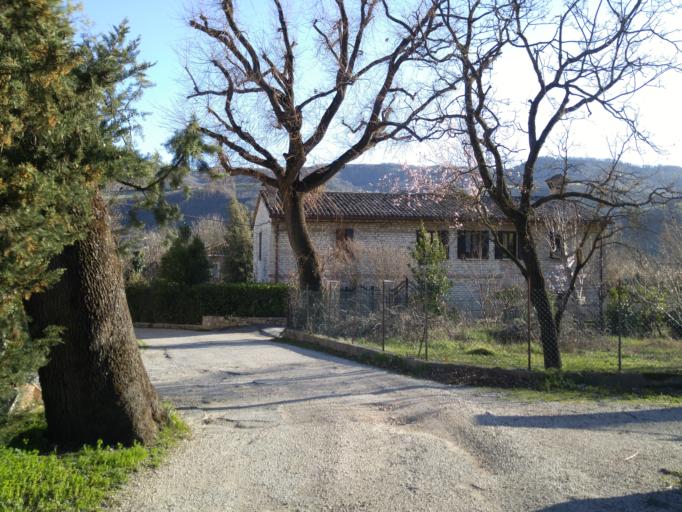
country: IT
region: The Marches
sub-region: Provincia di Pesaro e Urbino
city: Fossombrone
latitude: 43.6859
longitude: 12.7936
